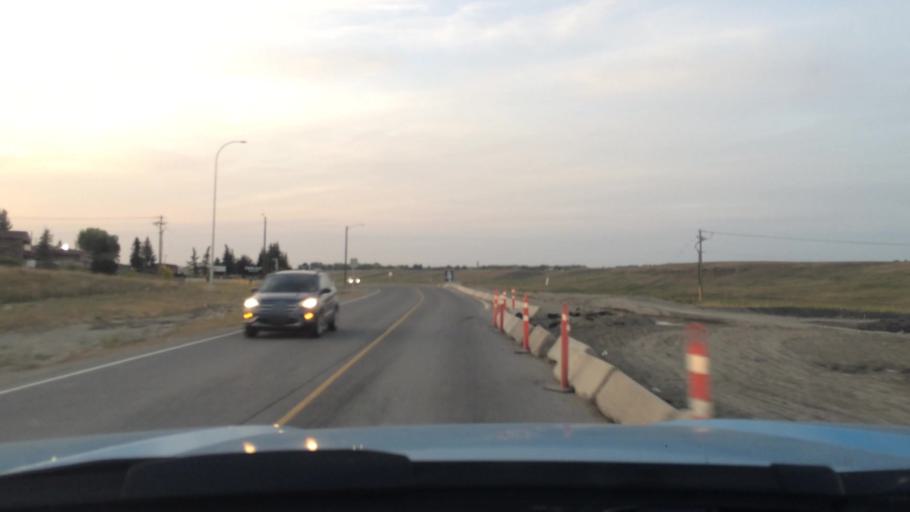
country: CA
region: Alberta
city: Calgary
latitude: 51.1821
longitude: -114.1346
